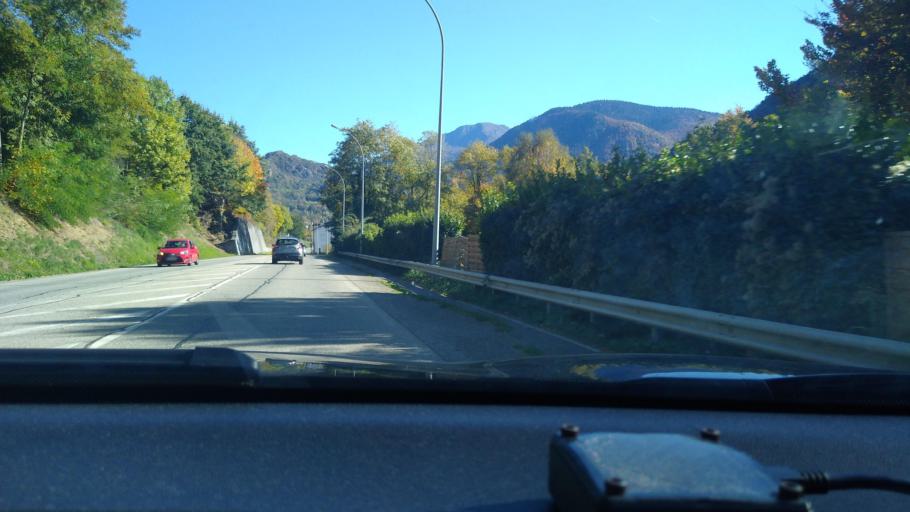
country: FR
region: Midi-Pyrenees
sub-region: Departement de l'Ariege
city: Ax-les-Thermes
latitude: 42.7283
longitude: 1.8269
